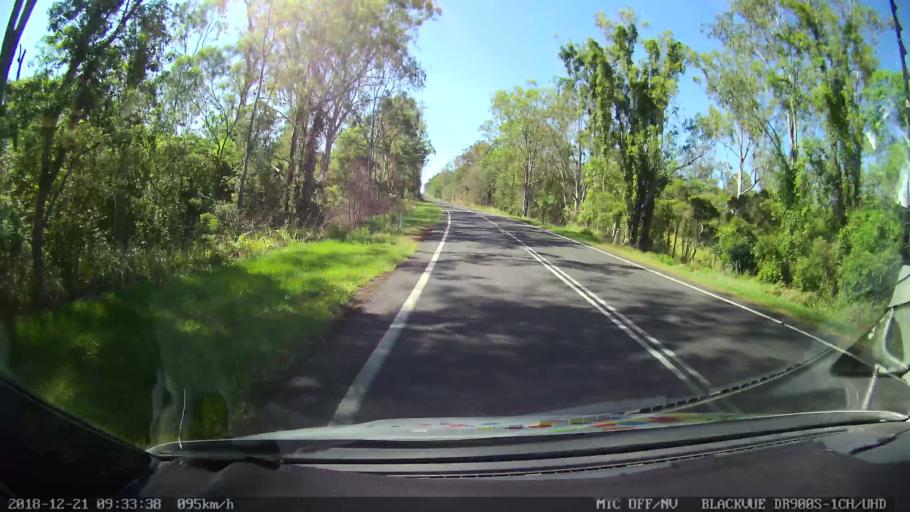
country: AU
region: New South Wales
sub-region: Clarence Valley
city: Grafton
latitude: -29.4873
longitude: 152.9766
